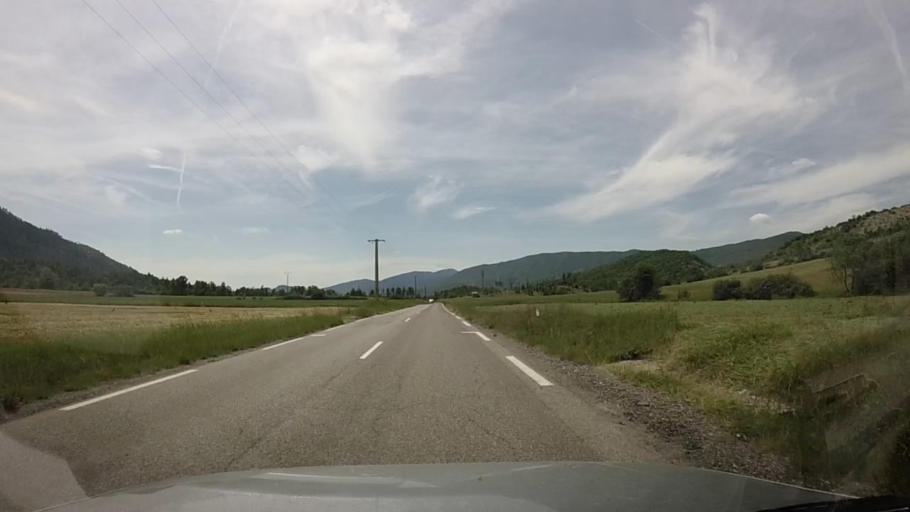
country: FR
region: Provence-Alpes-Cote d'Azur
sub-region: Departement des Alpes-de-Haute-Provence
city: Le Brusquet
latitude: 44.1667
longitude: 6.3275
